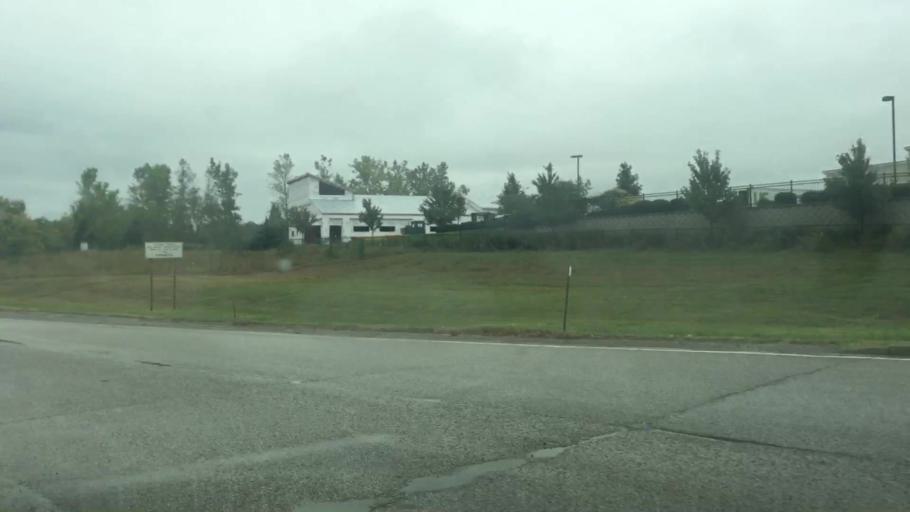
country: US
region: Kansas
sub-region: Johnson County
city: Lenexa
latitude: 38.9712
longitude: -94.7752
